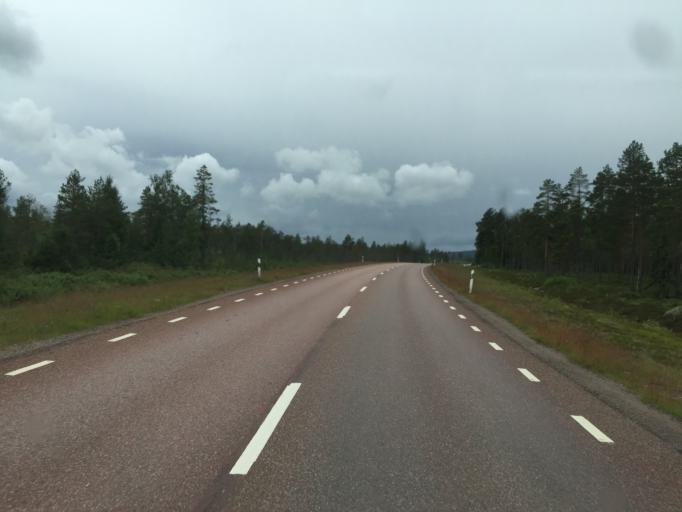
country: SE
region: Dalarna
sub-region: Malung-Saelens kommun
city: Malung
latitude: 60.6592
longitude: 13.6957
